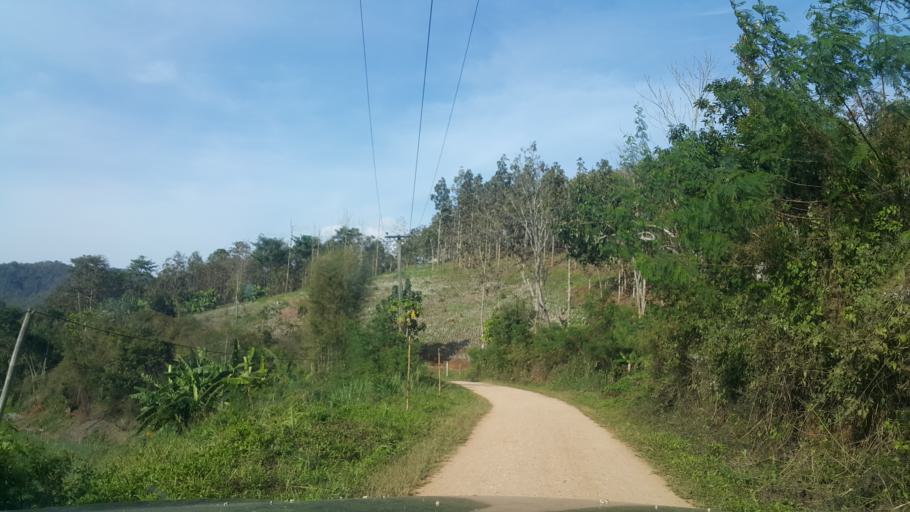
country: TH
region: Chiang Mai
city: Samoeng
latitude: 18.9514
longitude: 98.6758
